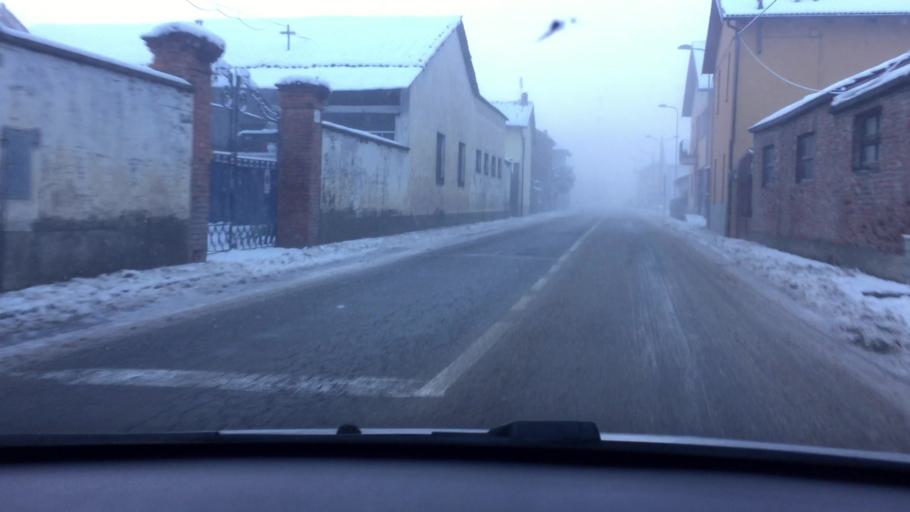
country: IT
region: Piedmont
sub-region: Provincia di Torino
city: Scalenghe
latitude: 44.8957
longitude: 7.4904
